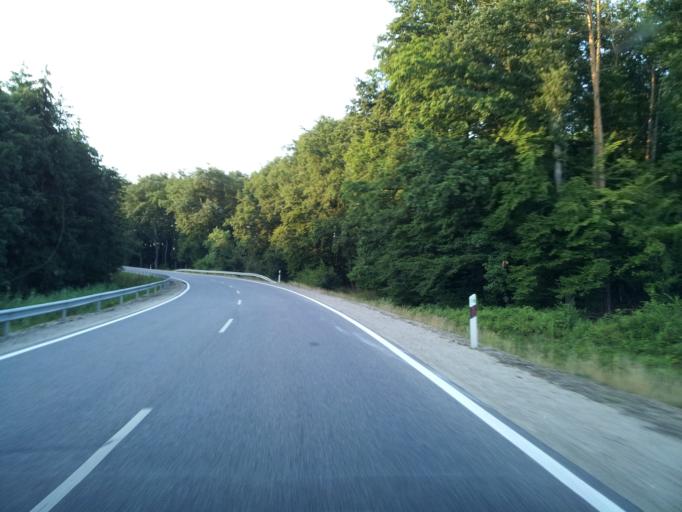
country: HU
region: Zala
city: Zalalovo
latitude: 46.7859
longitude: 16.5679
